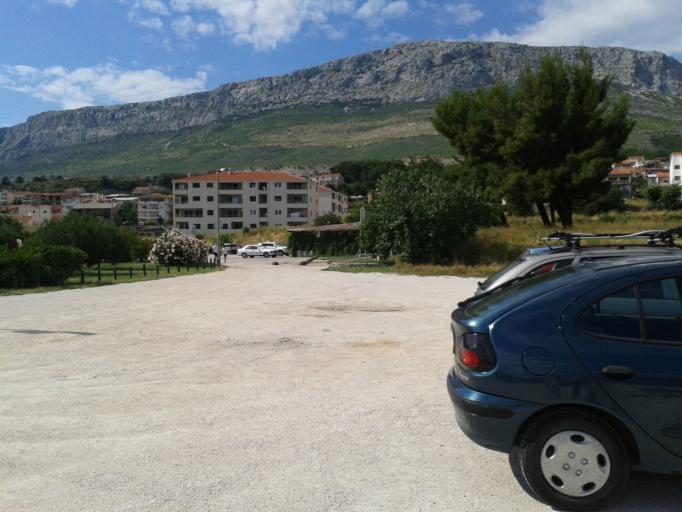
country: HR
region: Splitsko-Dalmatinska
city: Solin
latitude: 43.5418
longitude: 16.4815
